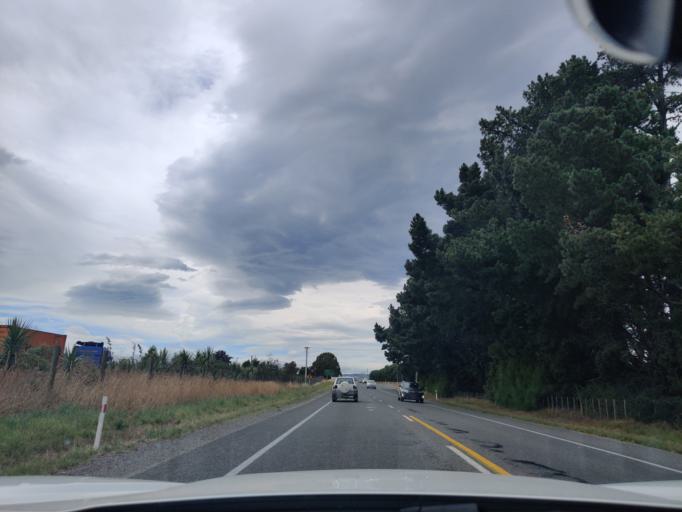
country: NZ
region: Wellington
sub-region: Masterton District
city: Masterton
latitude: -40.9729
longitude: 175.5977
